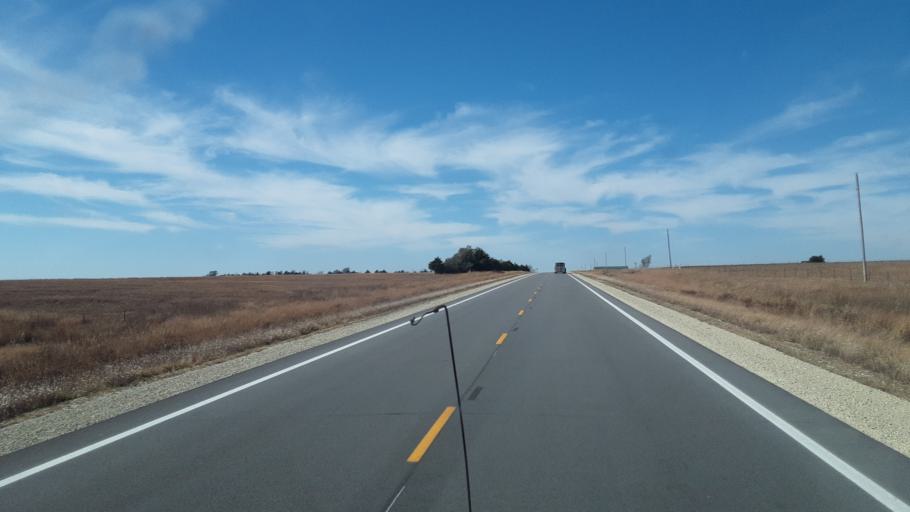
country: US
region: Kansas
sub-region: Marion County
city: Marion
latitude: 38.3628
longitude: -96.7932
